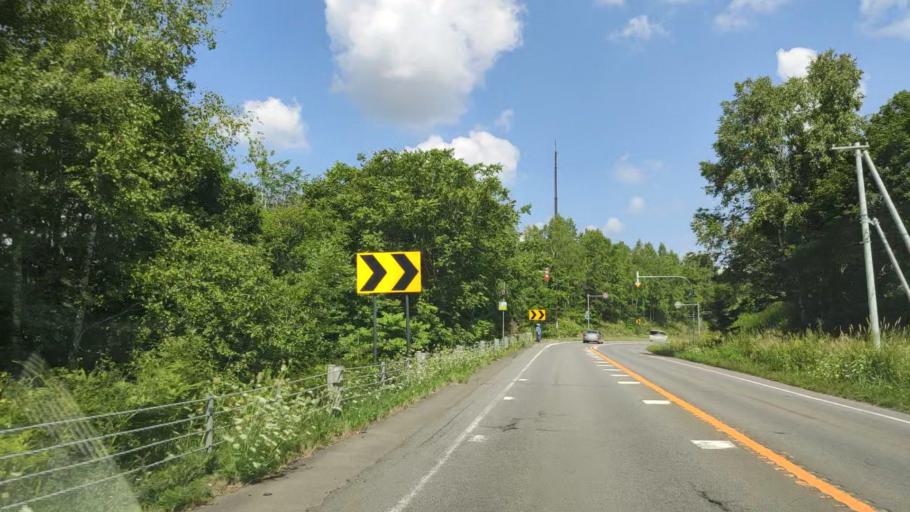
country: JP
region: Hokkaido
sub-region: Asahikawa-shi
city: Asahikawa
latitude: 43.5819
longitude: 142.4373
